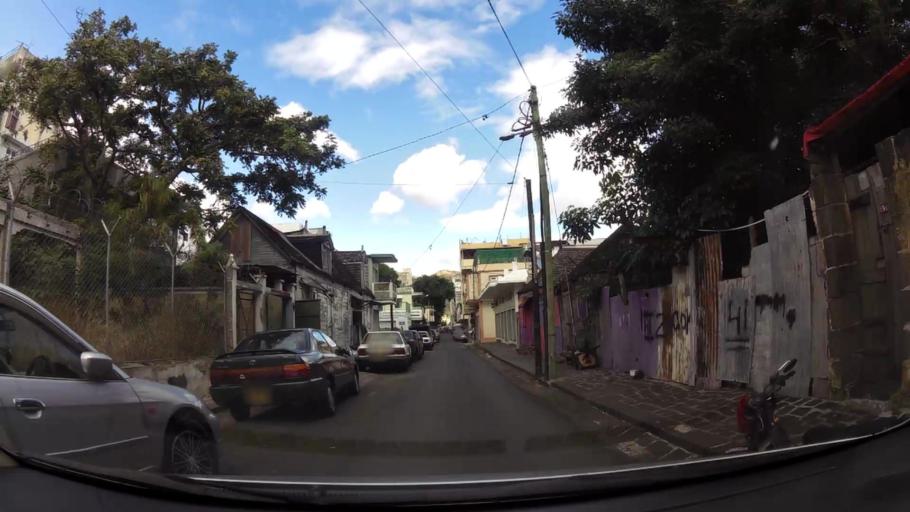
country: MU
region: Port Louis
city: Port Louis
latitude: -20.1564
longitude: 57.5081
